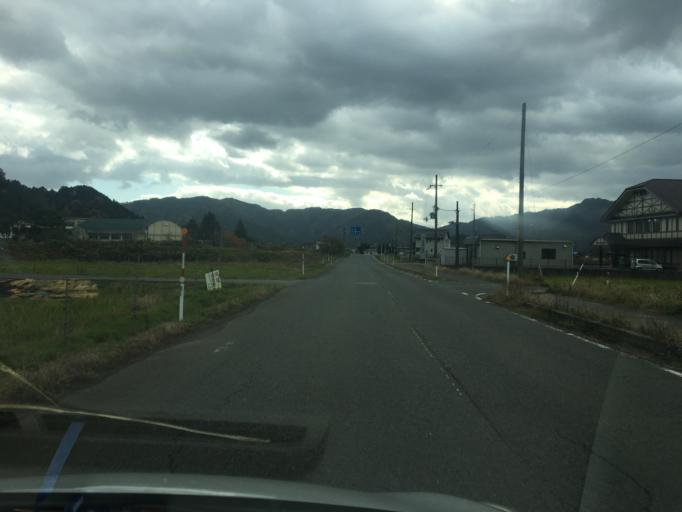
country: JP
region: Hyogo
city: Toyooka
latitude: 35.4736
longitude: 134.7191
